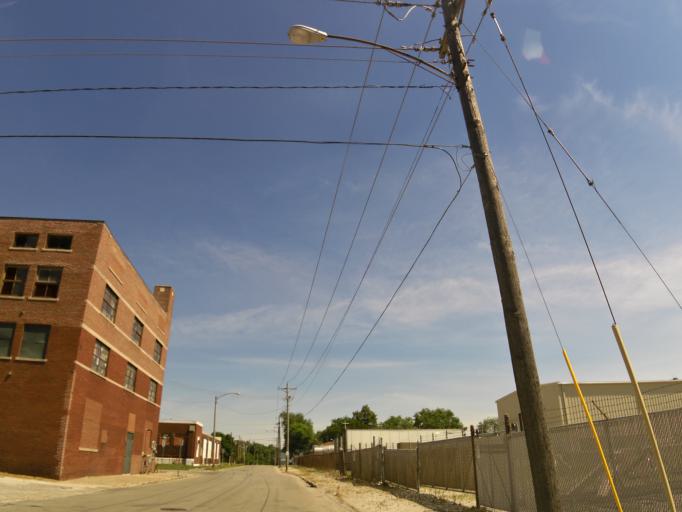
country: US
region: Illinois
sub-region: Vermilion County
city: Danville
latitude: 40.1277
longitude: -87.6261
